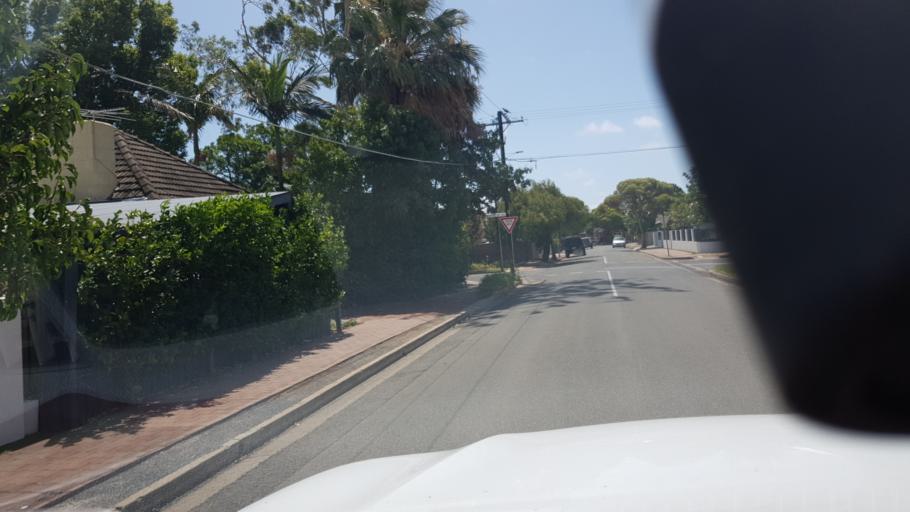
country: AU
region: South Australia
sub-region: Holdfast Bay
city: North Brighton
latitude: -34.9927
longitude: 138.5256
